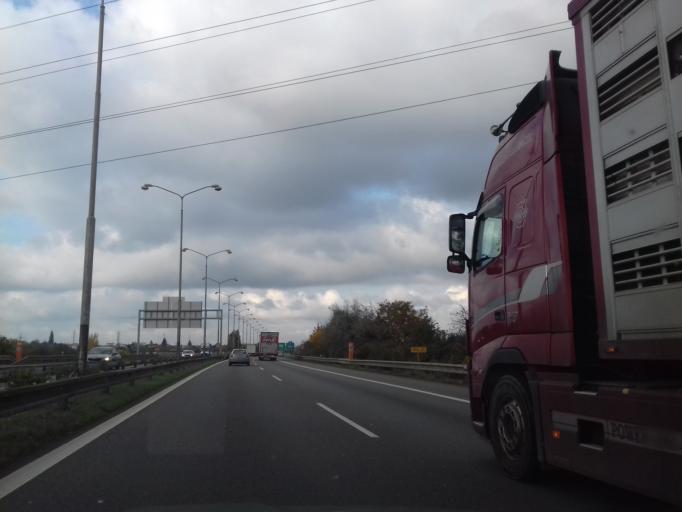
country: CZ
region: South Moravian
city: Moravany
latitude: 49.1590
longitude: 16.6106
